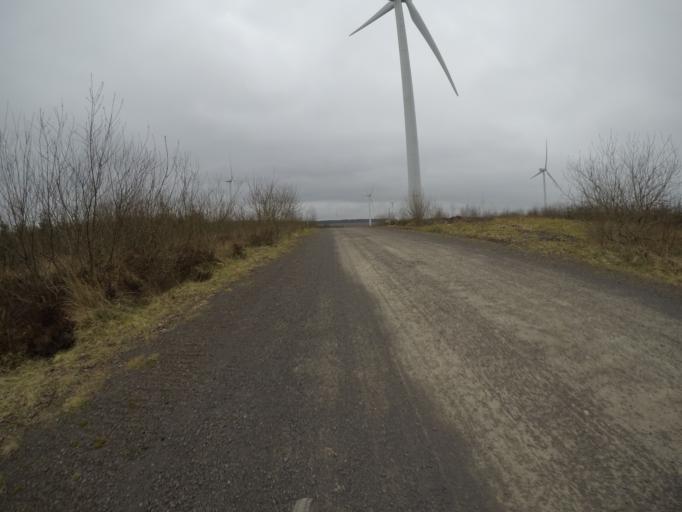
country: GB
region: Scotland
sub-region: East Ayrshire
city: Newmilns
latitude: 55.6557
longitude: -4.3245
